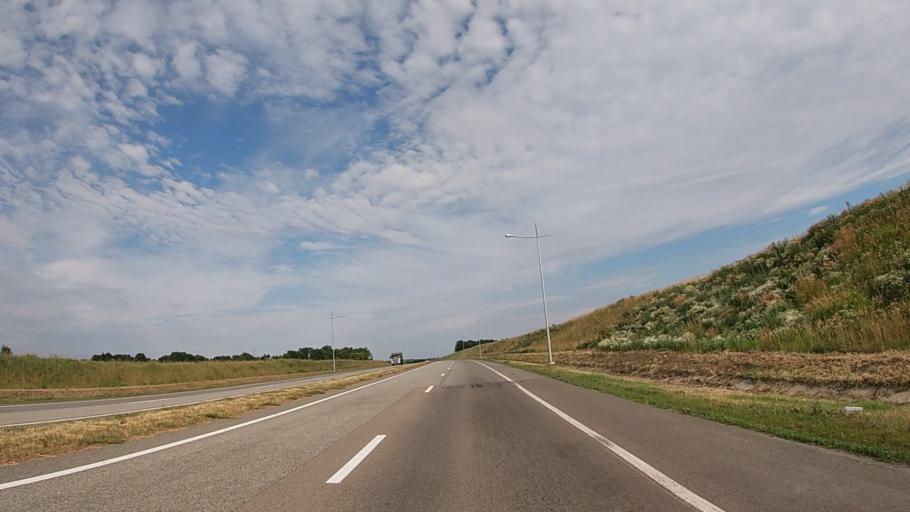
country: RU
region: Belgorod
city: Tomarovka
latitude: 50.7055
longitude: 36.2176
